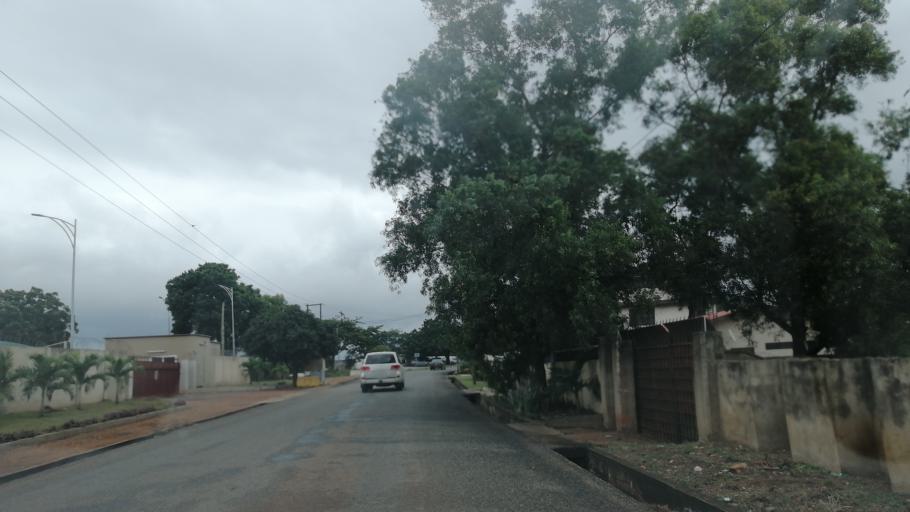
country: GH
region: Greater Accra
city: Medina Estates
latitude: 5.6330
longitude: -0.1535
